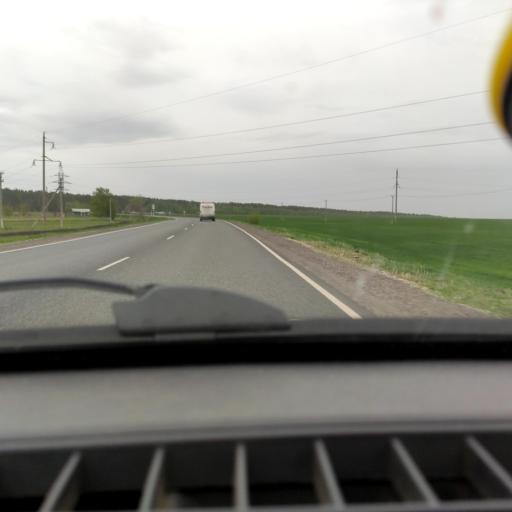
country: RU
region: Samara
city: Povolzhskiy
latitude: 53.6373
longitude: 49.6588
